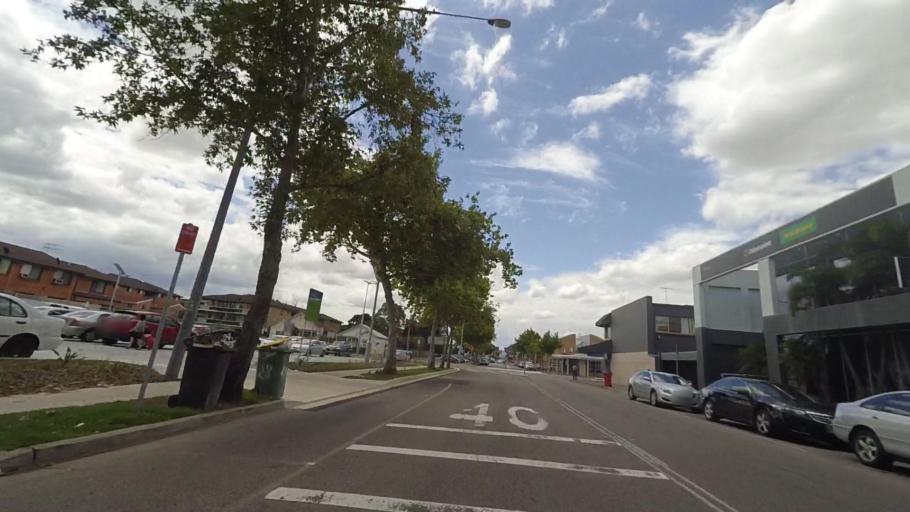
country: AU
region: New South Wales
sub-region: Fairfield
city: Carramar
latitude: -33.8729
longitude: 150.9531
